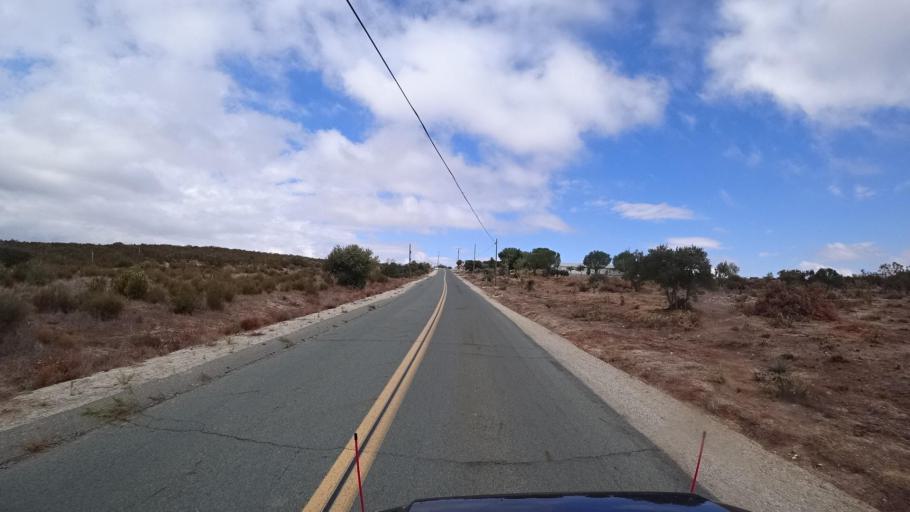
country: US
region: California
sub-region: San Diego County
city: Campo
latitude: 32.6375
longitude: -116.3203
